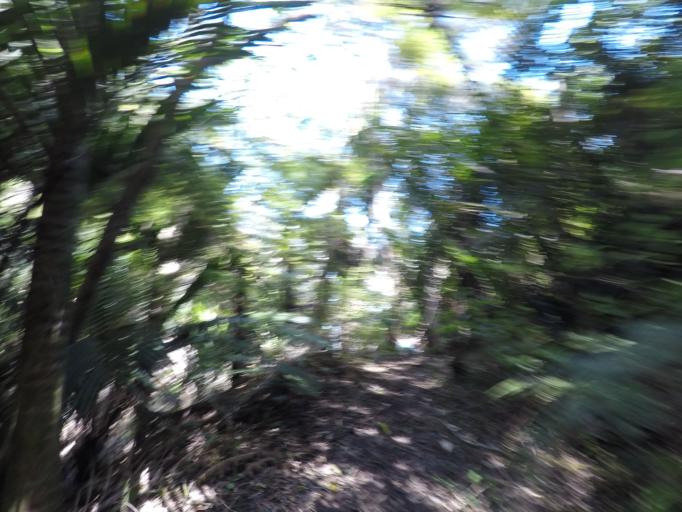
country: NZ
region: Auckland
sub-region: Auckland
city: Titirangi
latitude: -36.9766
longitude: 174.6307
